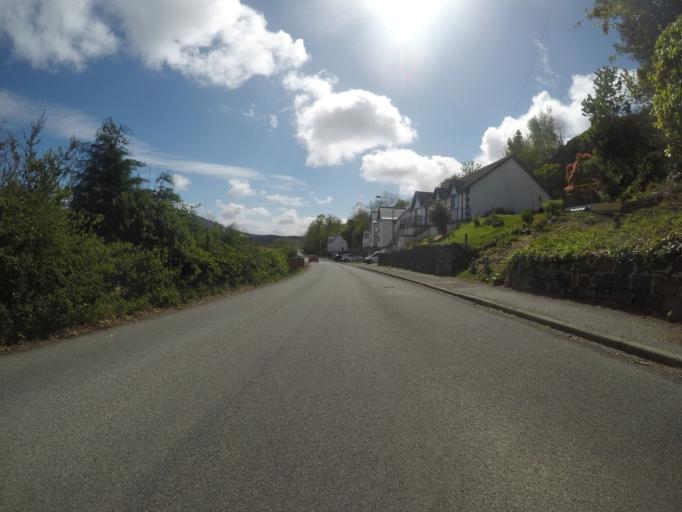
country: GB
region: Scotland
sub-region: Highland
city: Portree
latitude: 57.4162
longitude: -6.1911
